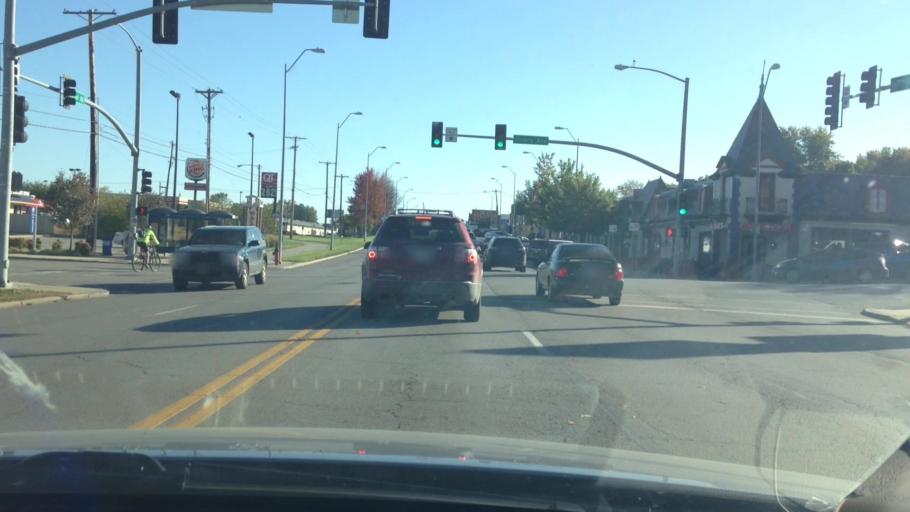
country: US
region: Kansas
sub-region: Johnson County
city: Mission Hills
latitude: 39.0000
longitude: -94.5938
